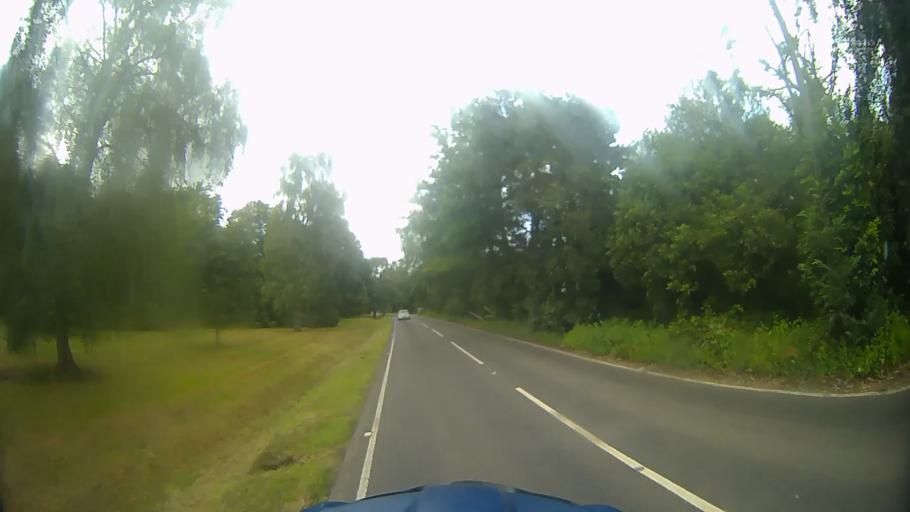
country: GB
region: England
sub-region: Wokingham
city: Barkham
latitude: 51.4122
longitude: -0.8758
